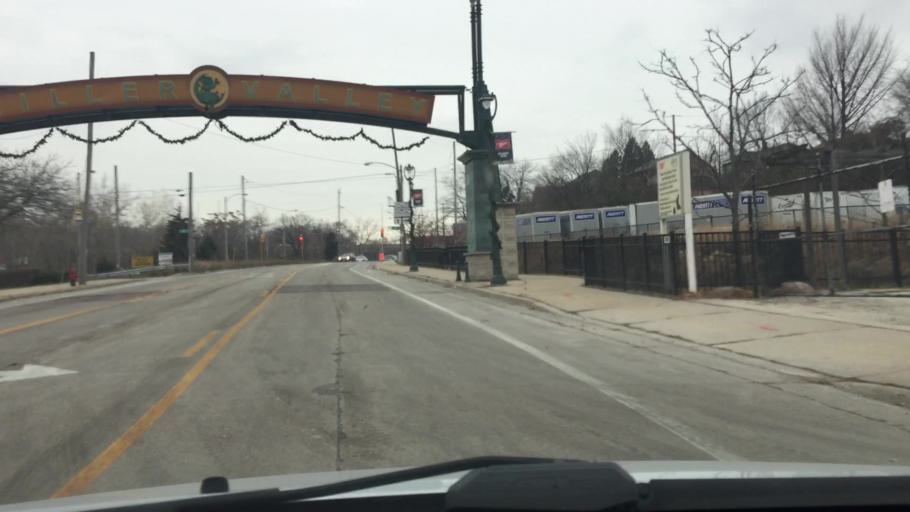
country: US
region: Wisconsin
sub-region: Milwaukee County
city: West Milwaukee
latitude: 43.0426
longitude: -87.9695
